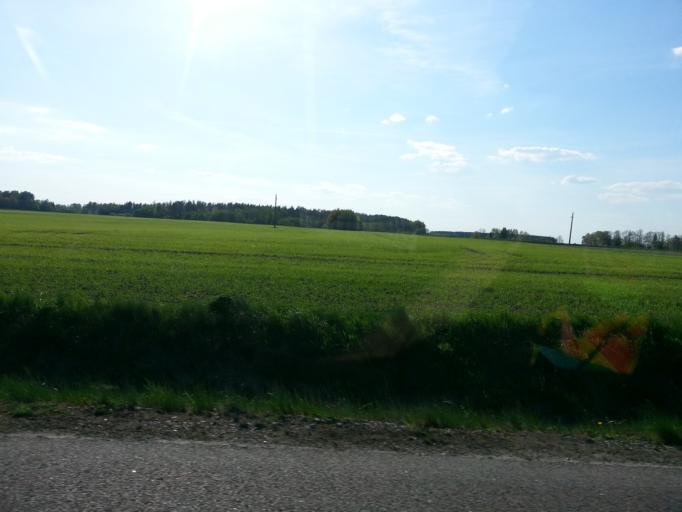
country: LT
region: Panevezys
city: Pasvalys
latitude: 55.9513
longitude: 24.3383
